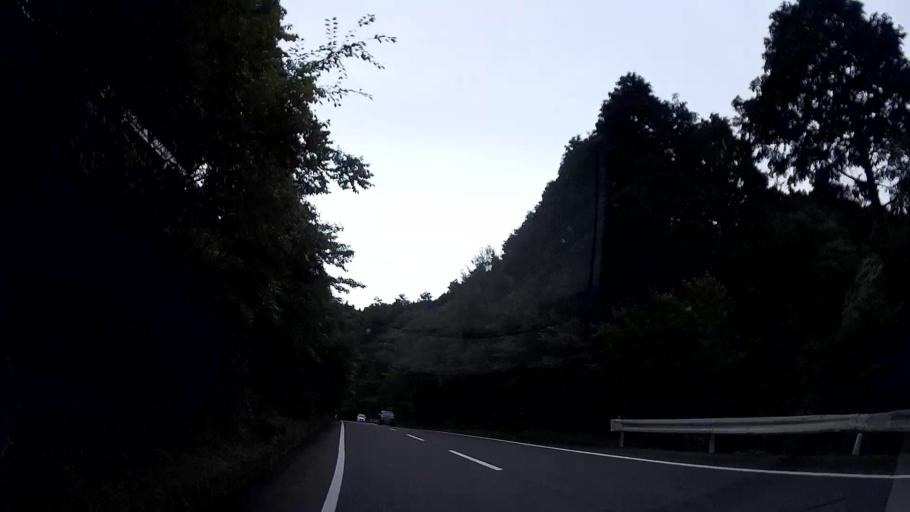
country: JP
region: Kumamoto
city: Kikuchi
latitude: 33.0710
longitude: 130.9137
